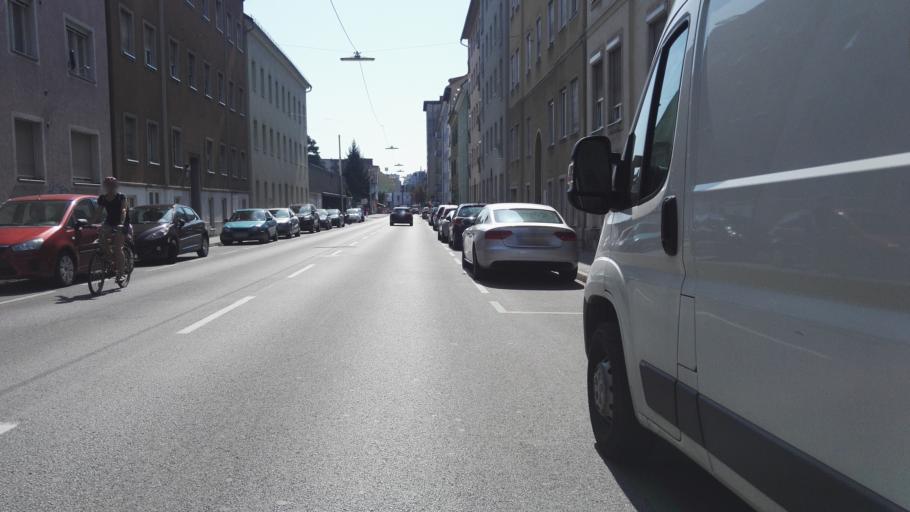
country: AT
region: Styria
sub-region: Graz Stadt
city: Goesting
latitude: 47.0829
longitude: 15.4202
